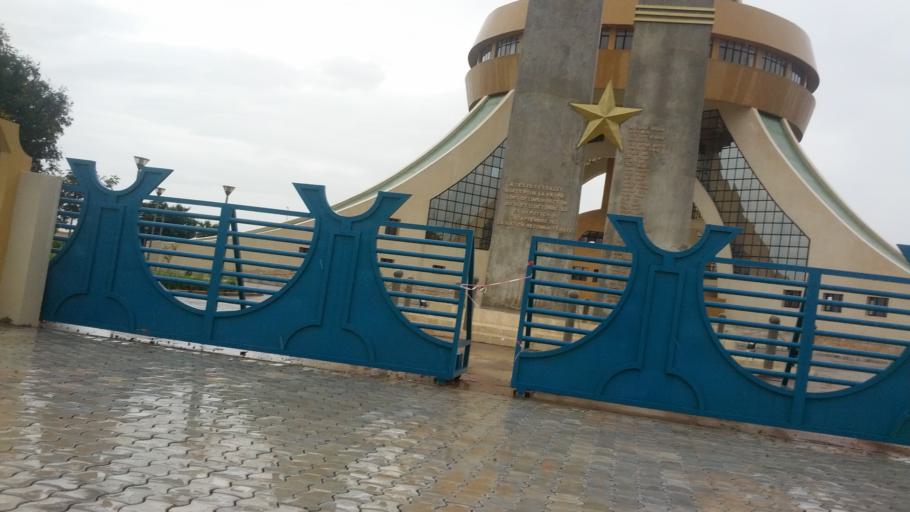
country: BF
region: Centre
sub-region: Kadiogo Province
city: Ouagadougou
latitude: 12.3115
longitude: -1.5026
